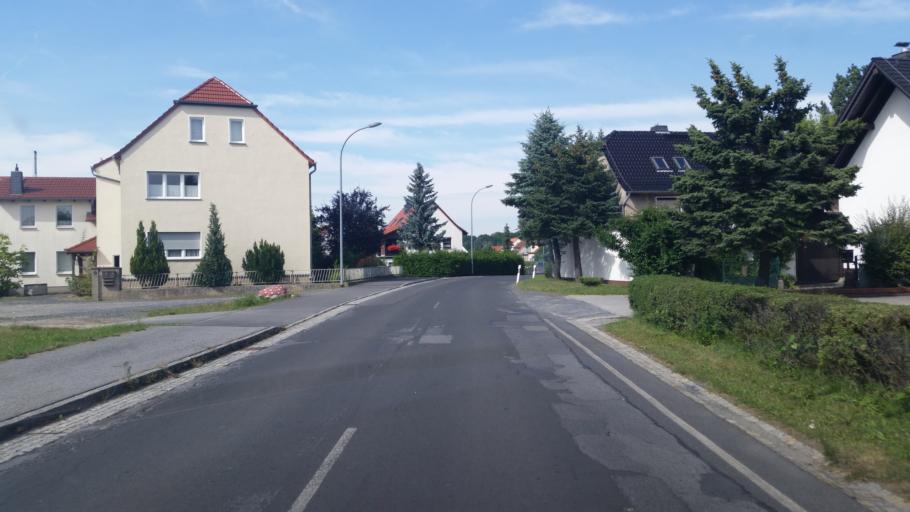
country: DE
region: Saxony
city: Bernsdorf
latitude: 51.3541
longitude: 14.0666
